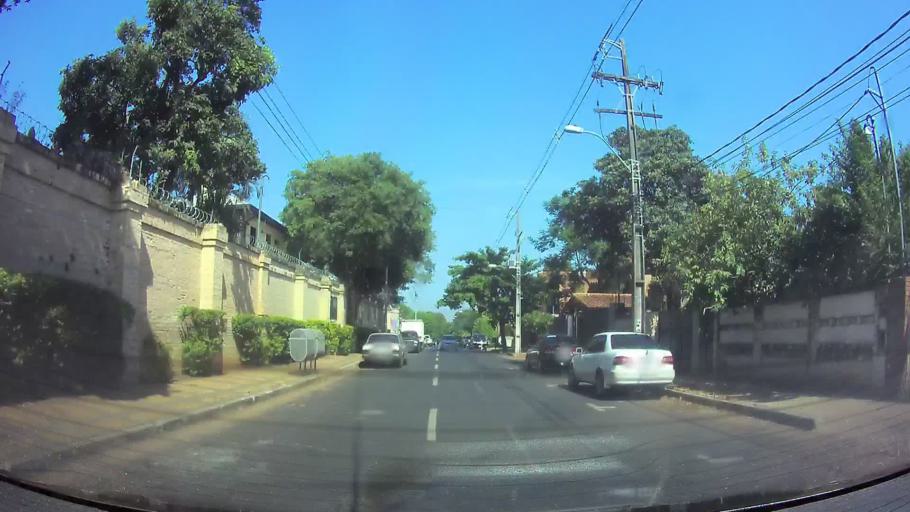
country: PY
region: Central
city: Fernando de la Mora
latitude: -25.2897
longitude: -57.5687
